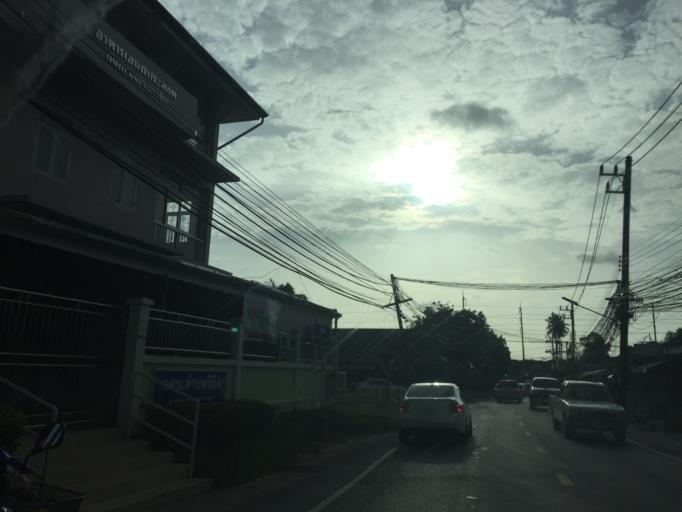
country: TH
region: Phuket
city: Mueang Phuket
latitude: 7.8587
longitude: 98.3790
